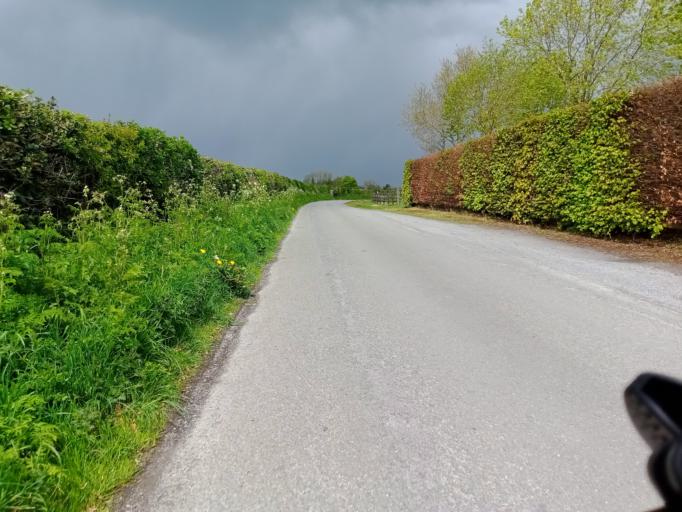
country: IE
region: Leinster
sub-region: Kilkenny
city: Kilkenny
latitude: 52.6807
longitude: -7.2669
